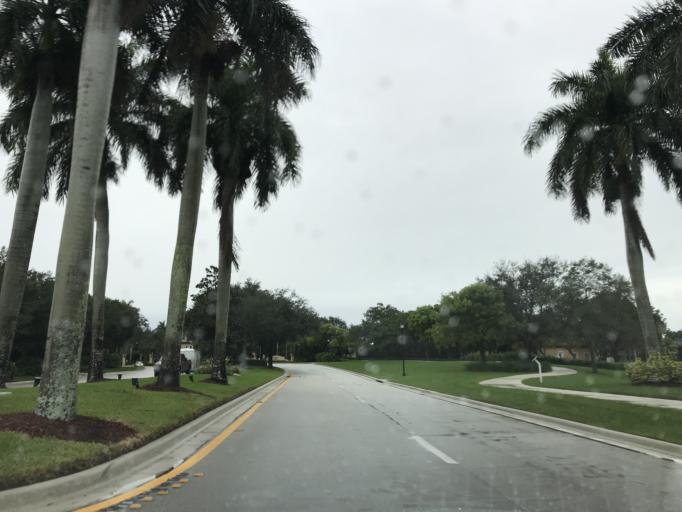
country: US
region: Florida
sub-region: Broward County
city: Coral Springs
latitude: 26.3072
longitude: -80.2846
